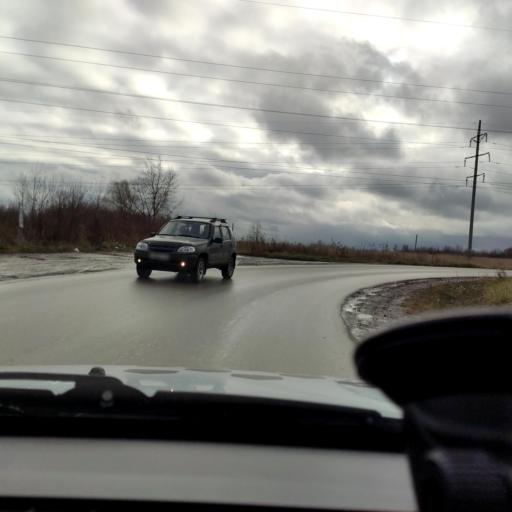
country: RU
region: Perm
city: Perm
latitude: 58.0188
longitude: 56.3378
